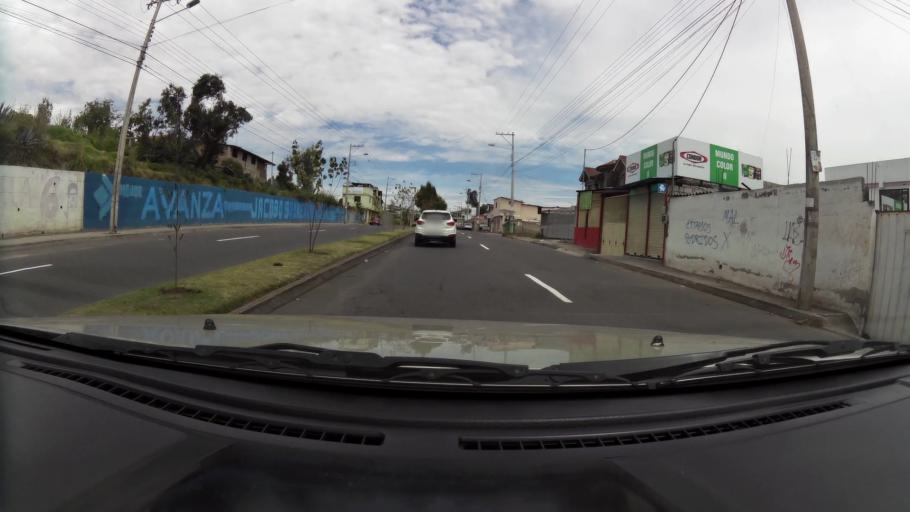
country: EC
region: Cotopaxi
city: San Miguel de Salcedo
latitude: -1.0765
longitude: -78.5957
